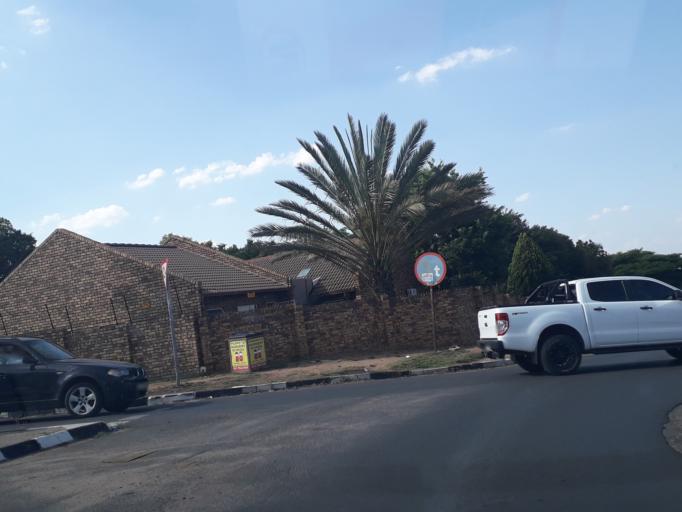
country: ZA
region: Gauteng
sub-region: West Rand District Municipality
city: Muldersdriseloop
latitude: -26.0775
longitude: 27.9285
